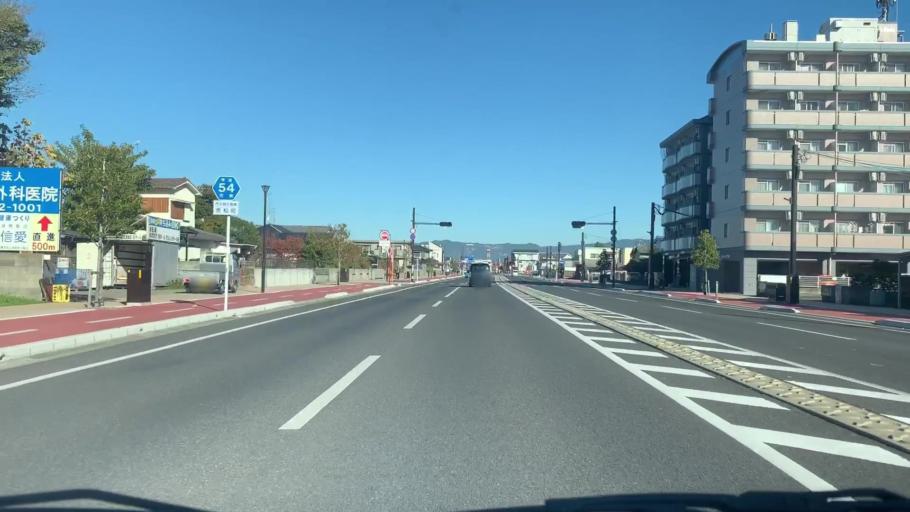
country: JP
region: Saga Prefecture
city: Saga-shi
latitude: 33.2461
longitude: 130.2931
